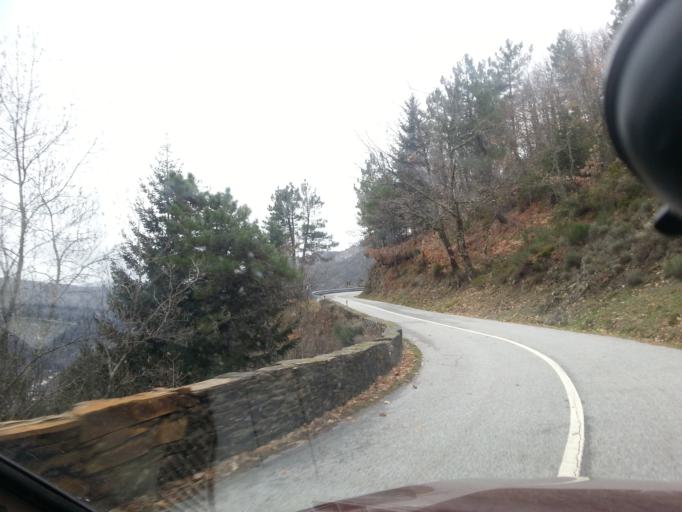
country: PT
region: Guarda
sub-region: Manteigas
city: Manteigas
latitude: 40.4146
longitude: -7.5434
